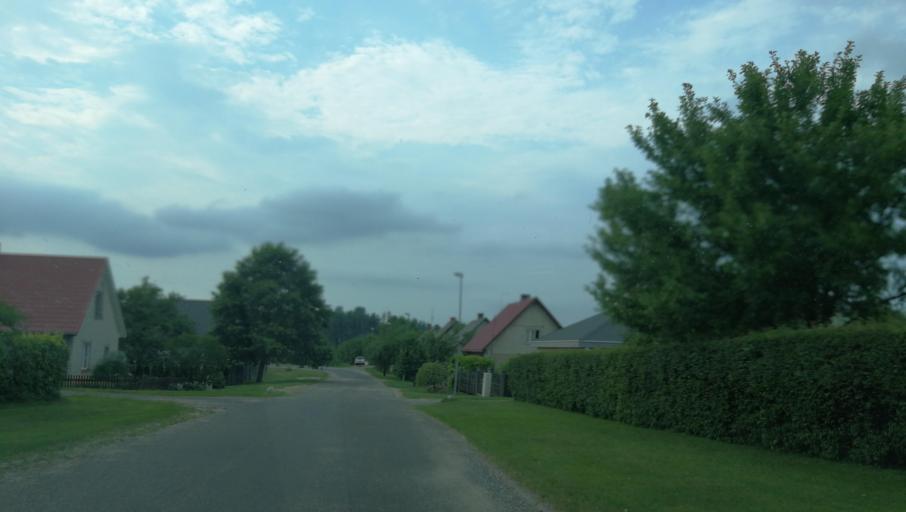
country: LV
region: Cesu Rajons
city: Cesis
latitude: 57.3199
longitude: 25.2733
